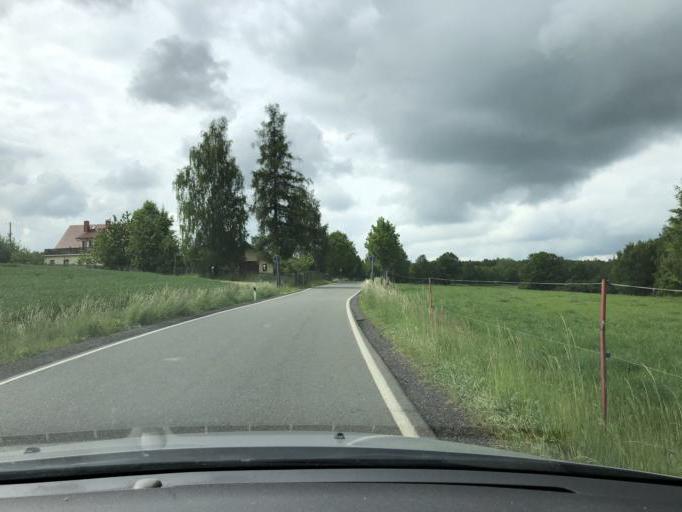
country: DE
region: Saxony
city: Waldenburg
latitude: 50.8587
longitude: 12.6006
